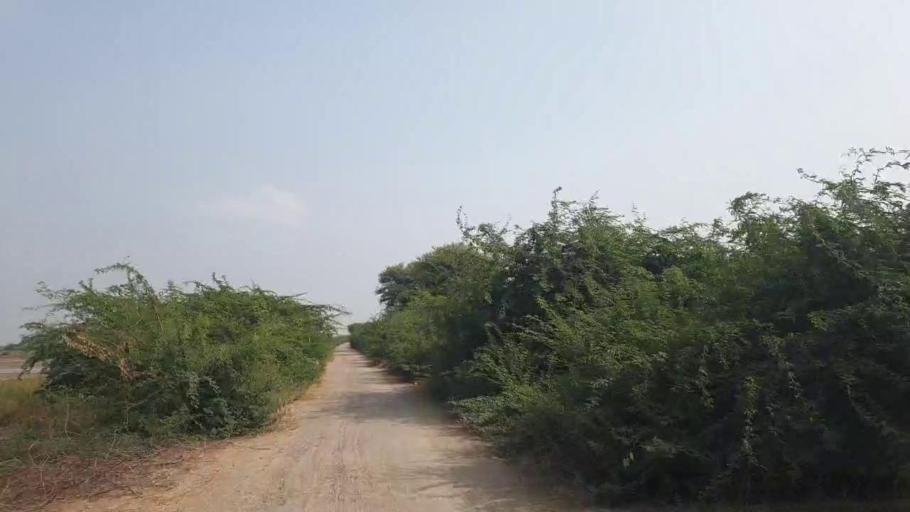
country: PK
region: Sindh
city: Badin
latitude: 24.5475
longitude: 68.6918
